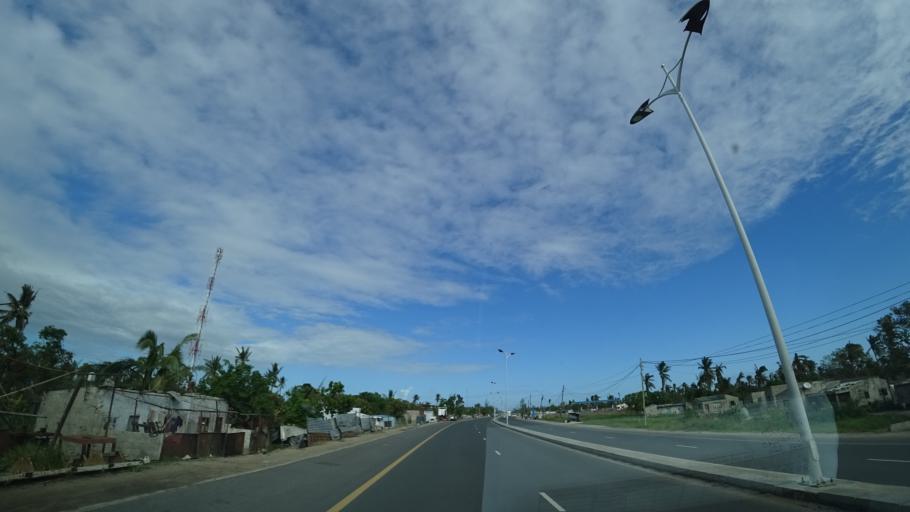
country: MZ
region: Sofala
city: Beira
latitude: -19.7517
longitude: 34.8754
